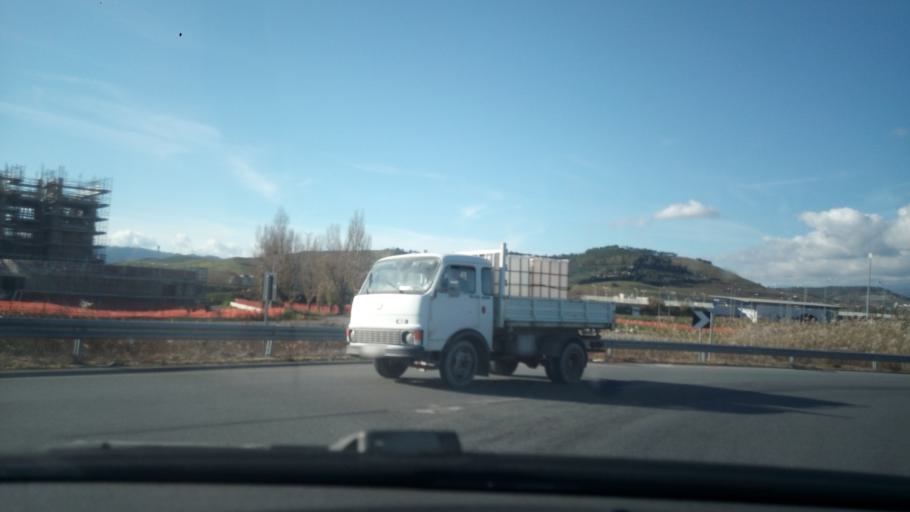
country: IT
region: Calabria
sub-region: Provincia di Catanzaro
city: Catanzaro
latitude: 38.8647
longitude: 16.5655
